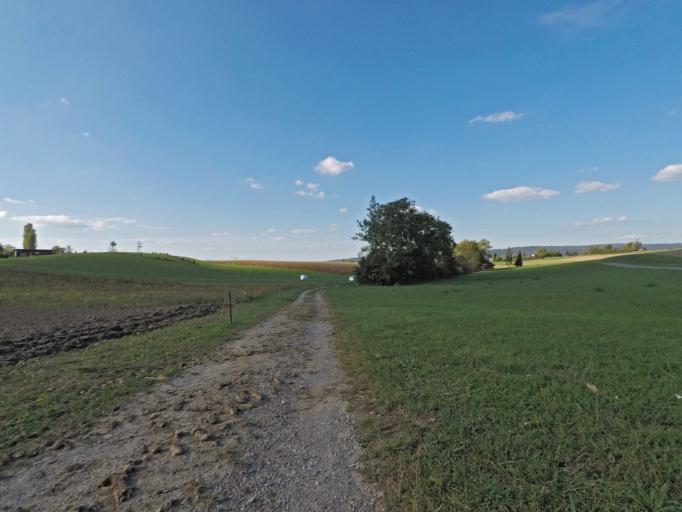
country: CH
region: Thurgau
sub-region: Frauenfeld District
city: Diessenhofen
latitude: 47.6600
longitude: 8.7470
